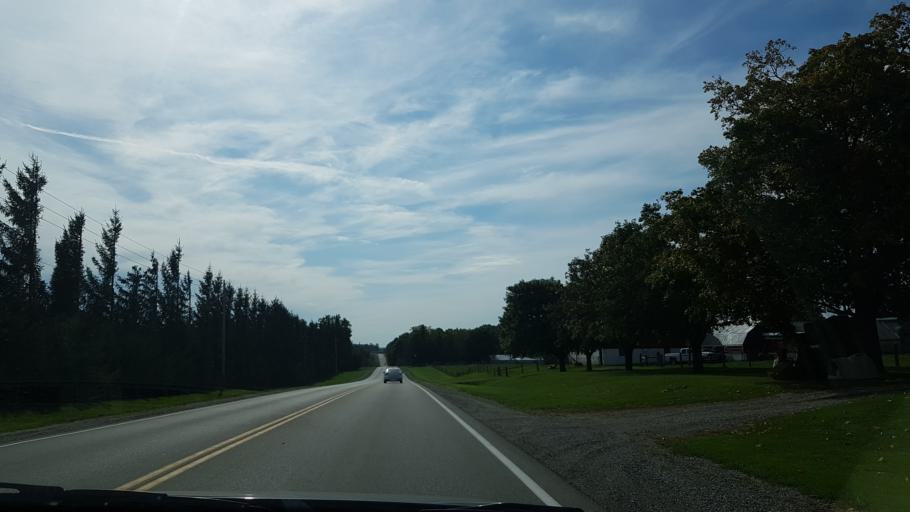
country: CA
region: Ontario
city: Delaware
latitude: 42.9680
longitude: -81.4000
